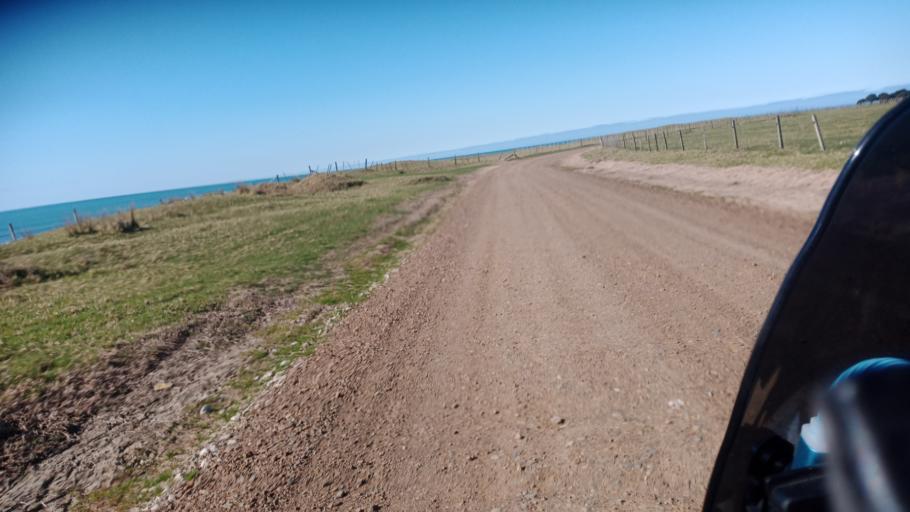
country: NZ
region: Gisborne
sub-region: Gisborne District
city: Gisborne
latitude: -39.0980
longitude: 177.9710
